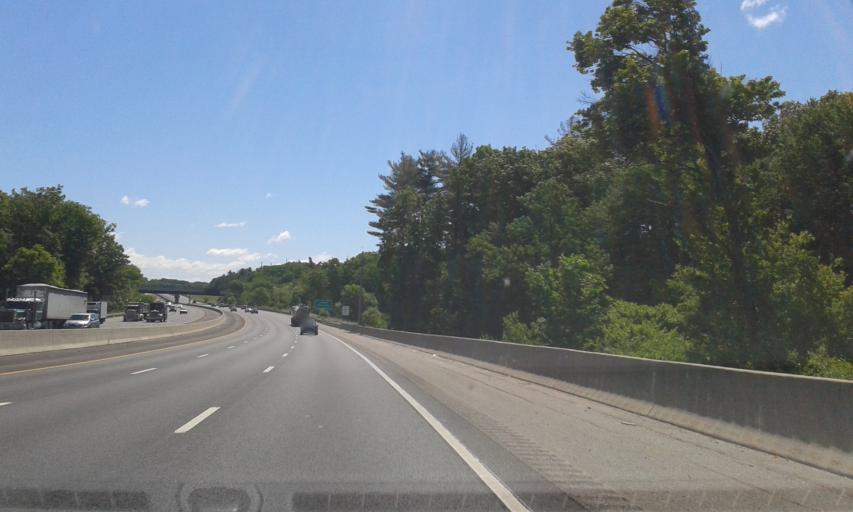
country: US
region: Massachusetts
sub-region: Middlesex County
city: Chelmsford
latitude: 42.6204
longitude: -71.3574
